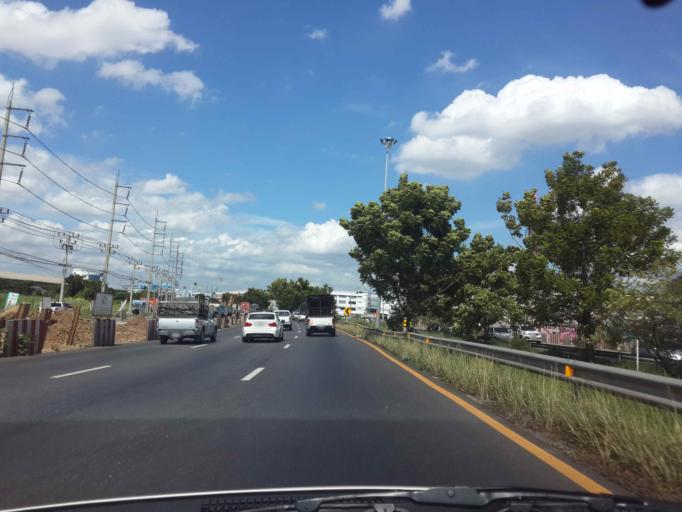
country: TH
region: Bangkok
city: Bang Bon
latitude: 13.5929
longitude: 100.3593
